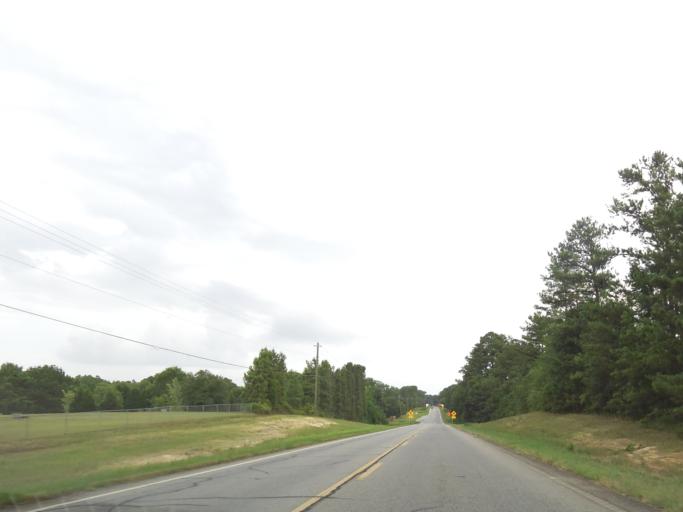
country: US
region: Georgia
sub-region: Bibb County
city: West Point
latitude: 32.8565
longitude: -83.7941
